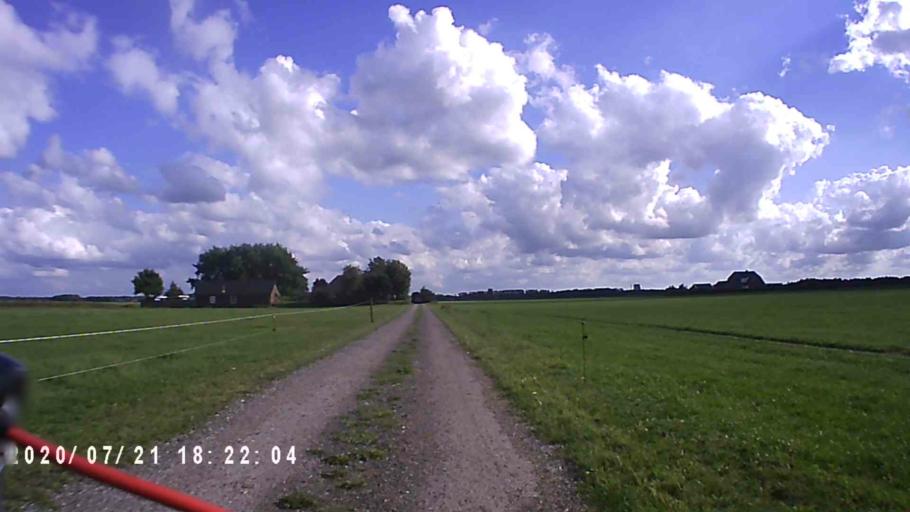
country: NL
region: Groningen
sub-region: Gemeente Hoogezand-Sappemeer
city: Hoogezand
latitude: 53.1860
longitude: 6.7677
